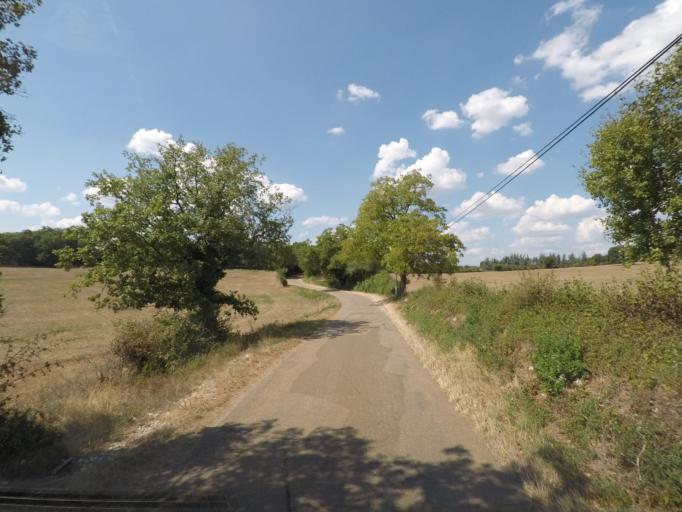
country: FR
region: Midi-Pyrenees
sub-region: Departement du Lot
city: Cahors
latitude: 44.5246
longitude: 1.6219
